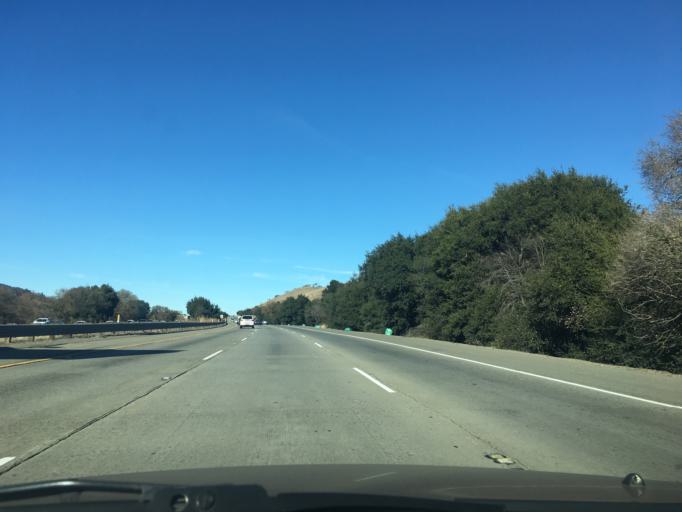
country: US
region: California
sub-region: Alameda County
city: Pleasanton
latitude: 37.6113
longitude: -121.8746
